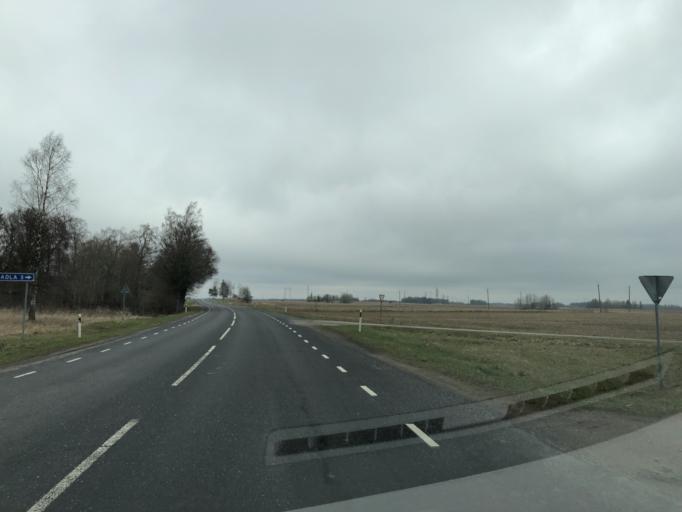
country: EE
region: Laeaene-Virumaa
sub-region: Vaeike-Maarja vald
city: Vaike-Maarja
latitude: 59.2096
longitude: 26.2704
